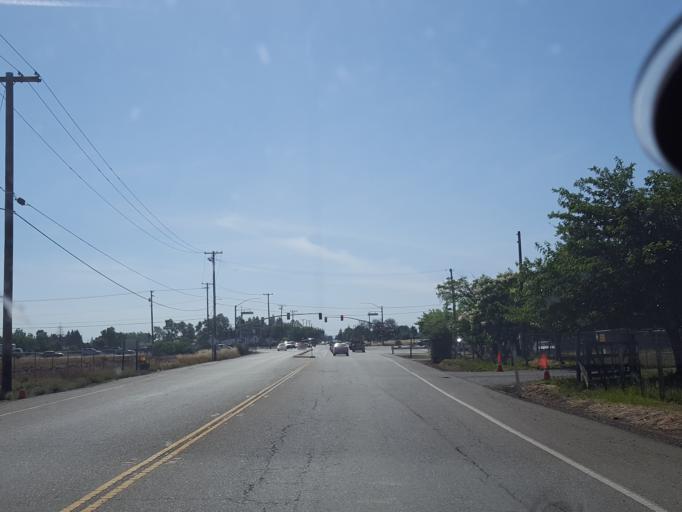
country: US
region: California
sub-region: Sacramento County
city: Florin
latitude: 38.4962
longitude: -121.3698
